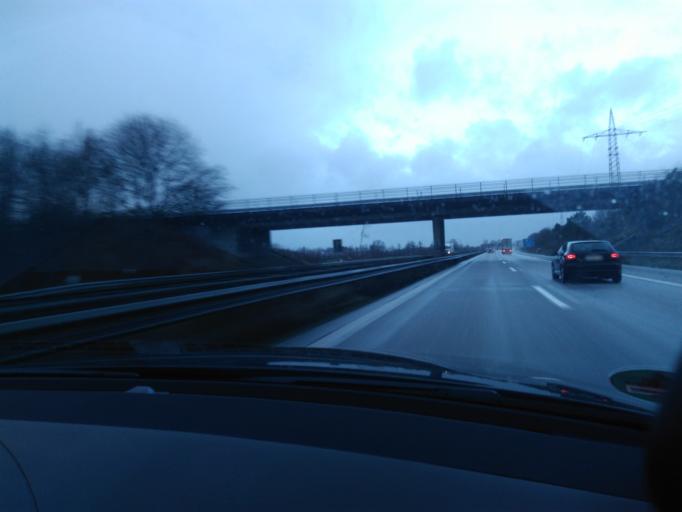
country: DE
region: Schleswig-Holstein
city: Padenstedt
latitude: 54.0545
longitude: 9.9252
